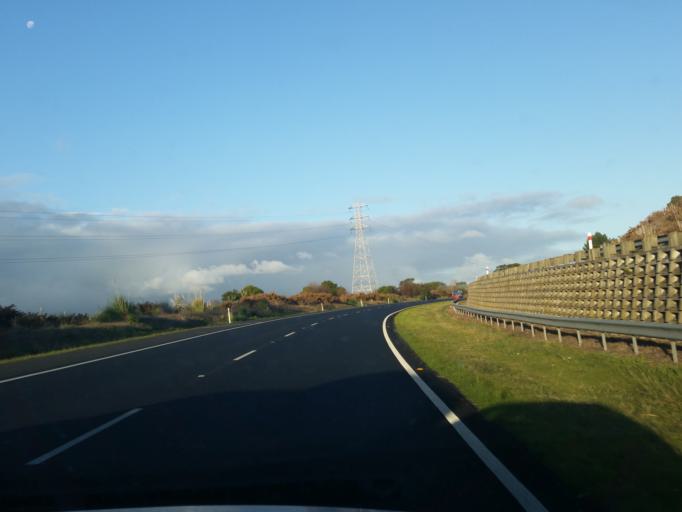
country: NZ
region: Auckland
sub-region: Auckland
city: Pukekohe East
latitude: -37.2533
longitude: 175.0353
